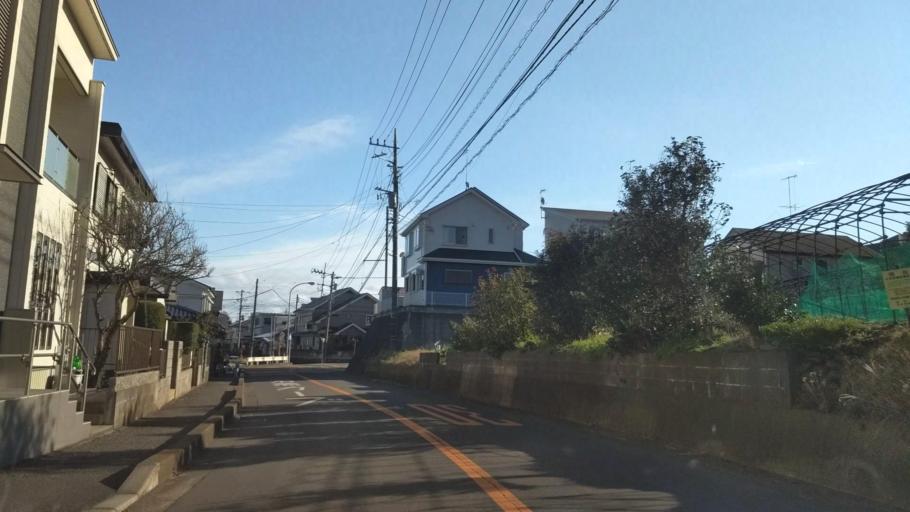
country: JP
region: Kanagawa
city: Hadano
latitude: 35.3644
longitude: 139.2520
